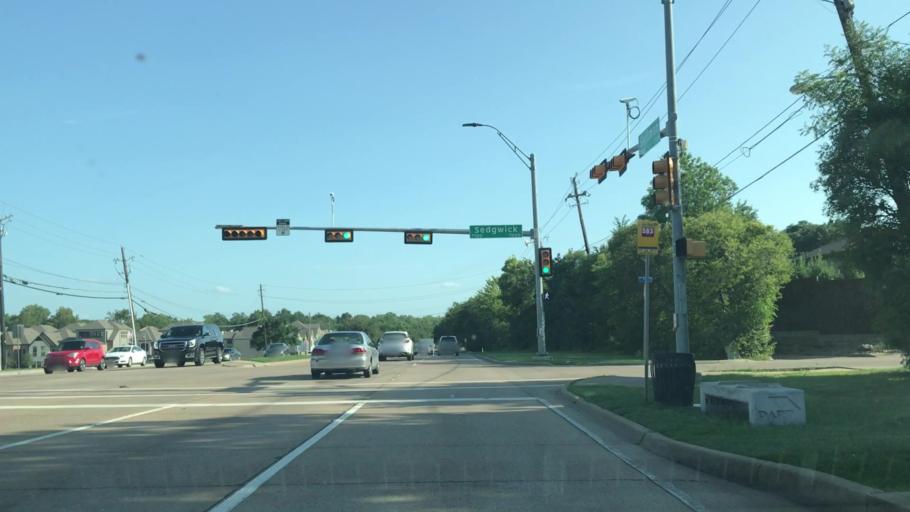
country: US
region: Texas
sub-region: Dallas County
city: University Park
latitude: 32.8760
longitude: -96.7349
